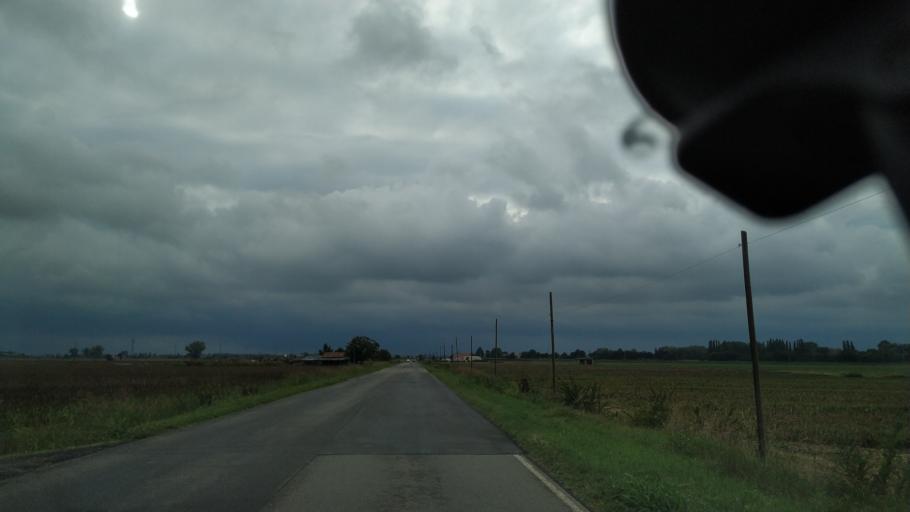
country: IT
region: Emilia-Romagna
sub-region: Provincia di Bologna
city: Decima
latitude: 44.7075
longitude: 11.2020
